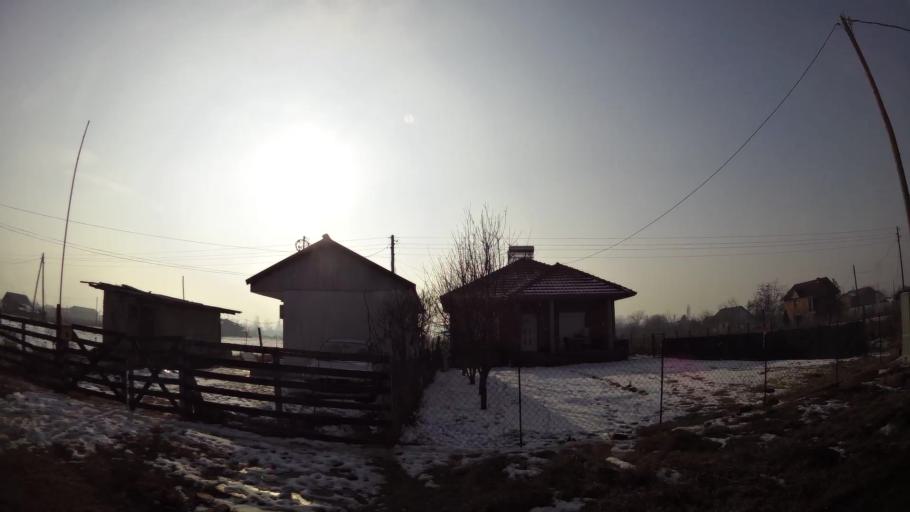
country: MK
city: Kadino
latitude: 41.9627
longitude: 21.5989
